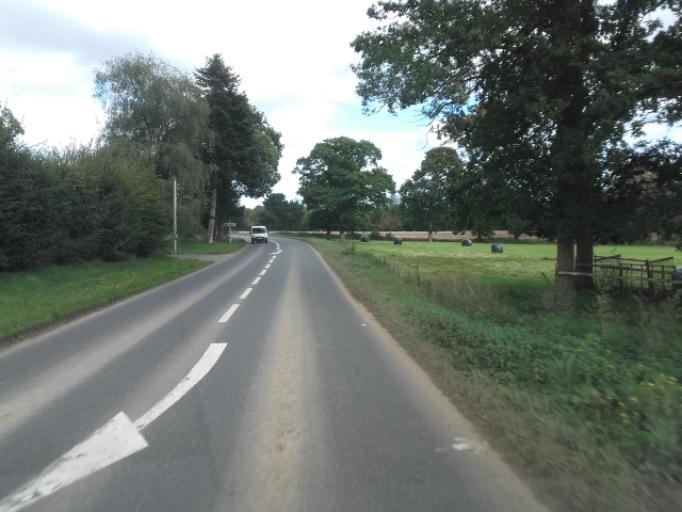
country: FR
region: Brittany
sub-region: Departement des Cotes-d'Armor
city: Lanvollon
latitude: 48.6457
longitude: -2.9661
